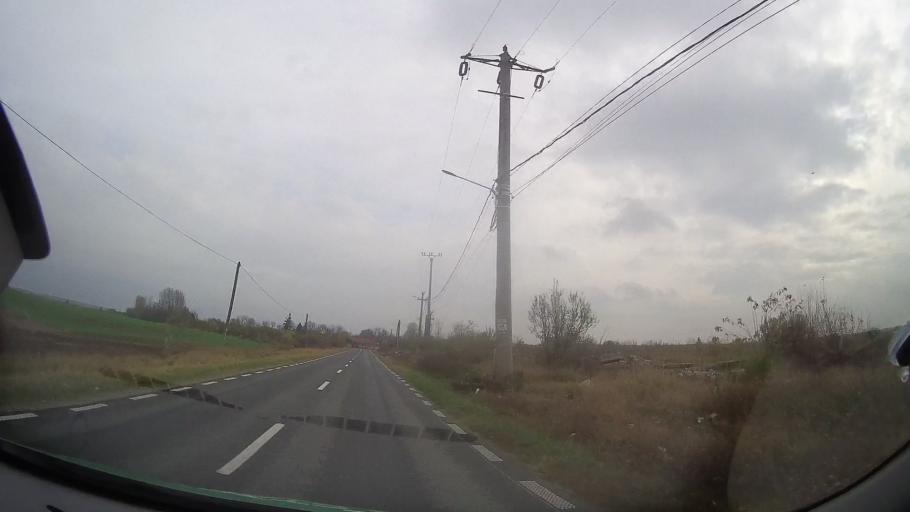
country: RO
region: Ilfov
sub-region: Comuna Gruiu
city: Lipia
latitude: 44.7185
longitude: 26.2718
